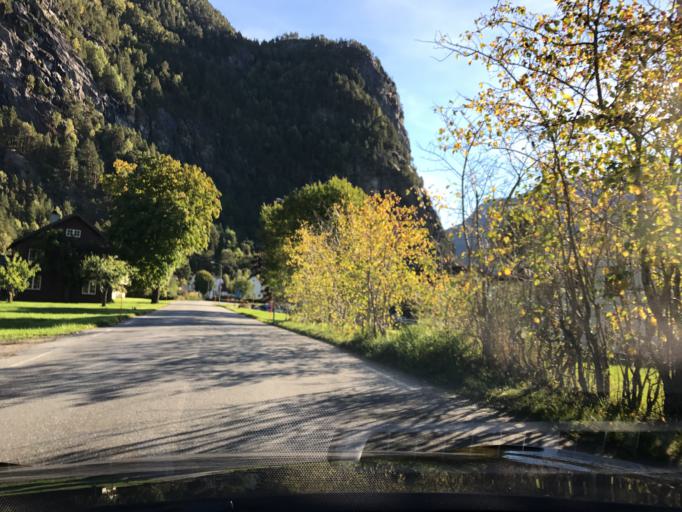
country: NO
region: More og Romsdal
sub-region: Norddal
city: Valldal
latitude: 62.3009
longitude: 7.2588
